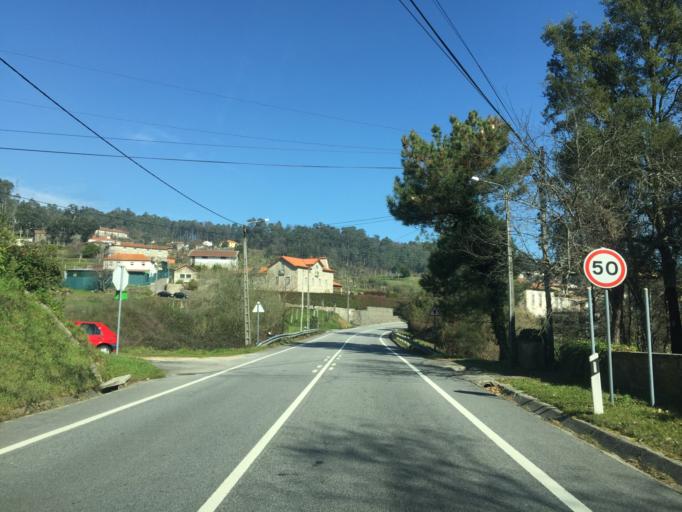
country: PT
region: Aveiro
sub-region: Vale de Cambra
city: Macieira de Cambra
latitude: 40.8837
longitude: -8.3638
